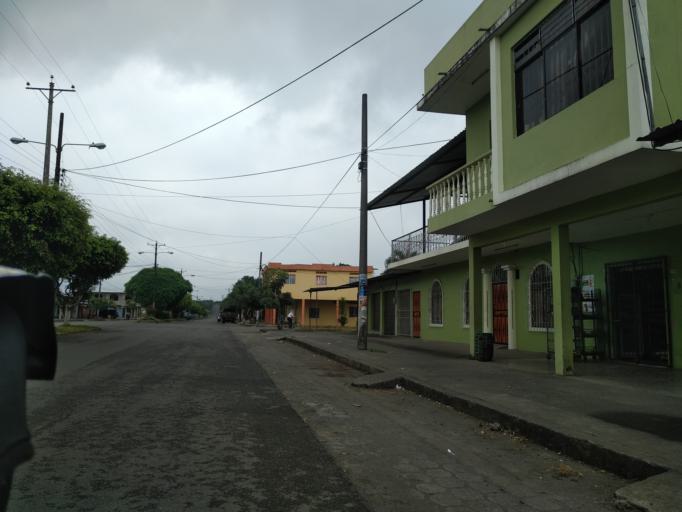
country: EC
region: Cotopaxi
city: La Mana
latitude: -0.9554
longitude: -79.3508
